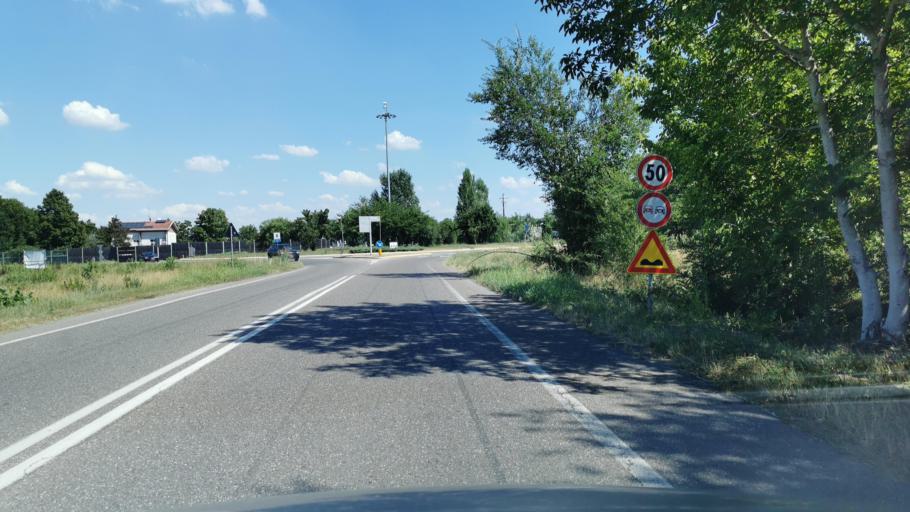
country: IT
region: Emilia-Romagna
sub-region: Provincia di Modena
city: Sam Marino
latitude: 44.8016
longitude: 10.9030
